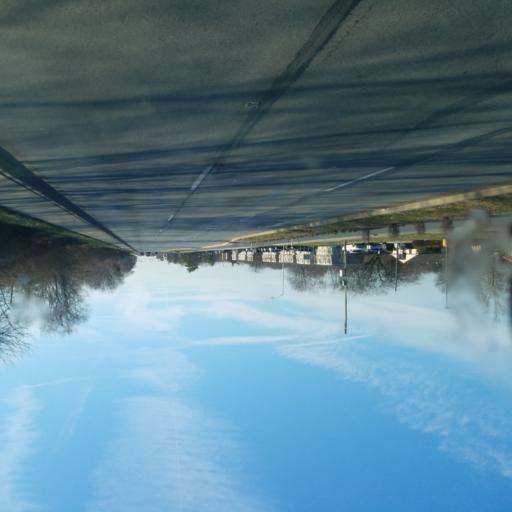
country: US
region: Indiana
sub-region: Marion County
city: Speedway
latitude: 39.8235
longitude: -86.2674
